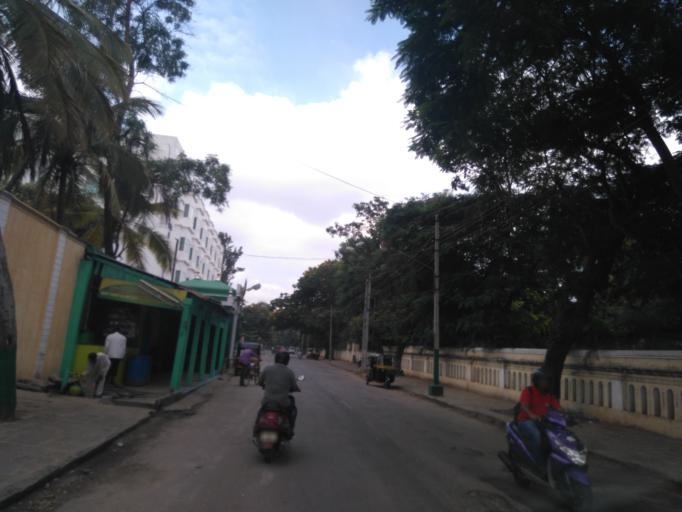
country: IN
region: Karnataka
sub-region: Mysore
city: Mysore
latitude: 12.3079
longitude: 76.6460
